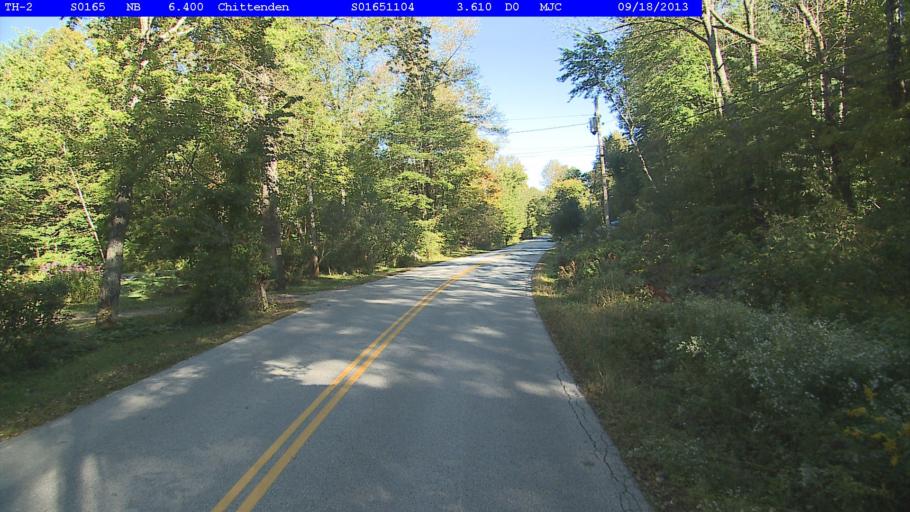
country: US
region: Vermont
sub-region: Rutland County
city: Rutland
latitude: 43.7261
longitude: -72.9698
